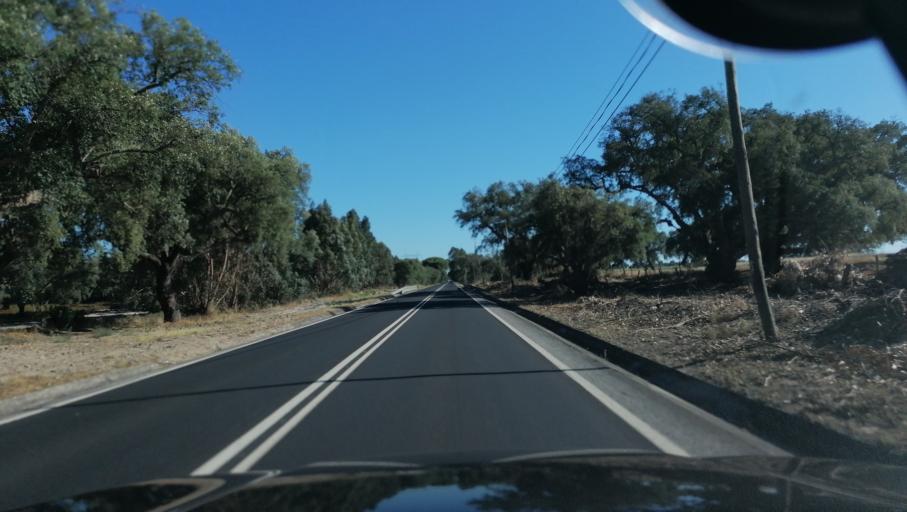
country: PT
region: Santarem
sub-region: Benavente
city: Samora Correia
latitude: 38.8576
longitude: -8.8811
